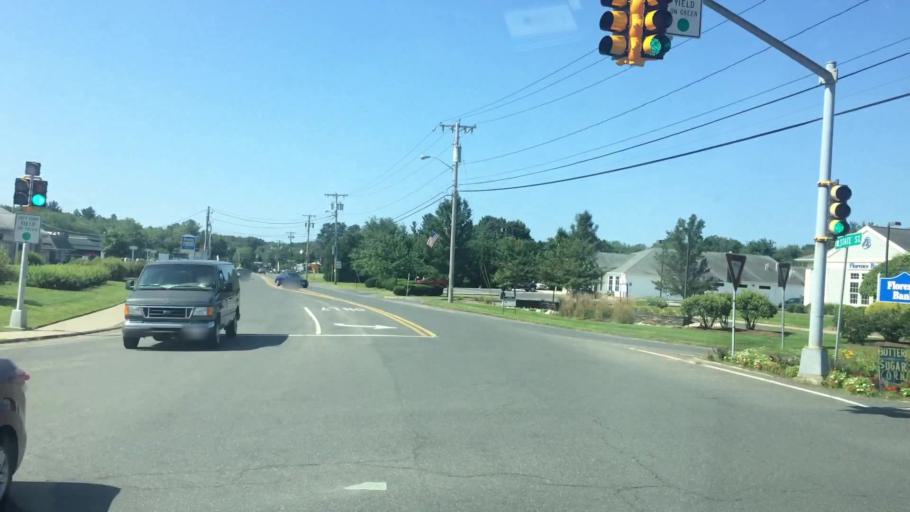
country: US
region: Massachusetts
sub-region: Hampshire County
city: Granby
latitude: 42.2468
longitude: -72.5443
